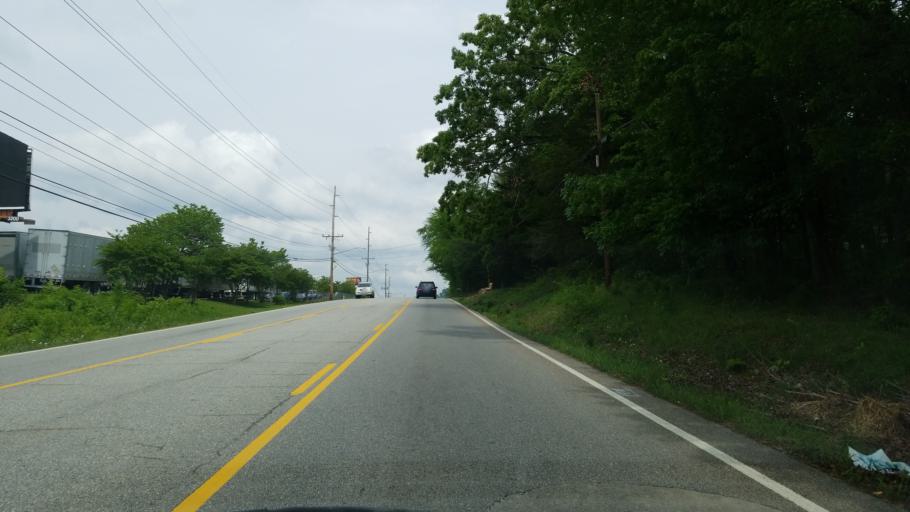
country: US
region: Tennessee
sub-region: Hamilton County
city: Harrison
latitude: 35.0550
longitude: -85.1445
